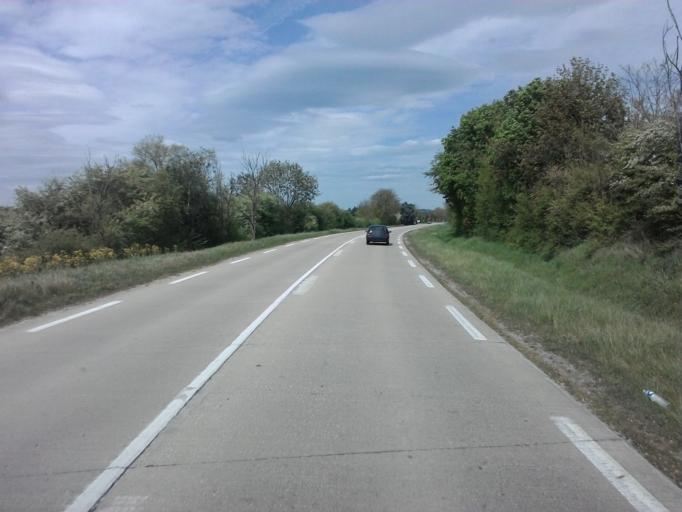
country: FR
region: Bourgogne
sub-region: Departement de l'Yonne
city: Champs-sur-Yonne
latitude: 47.7475
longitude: 3.6036
